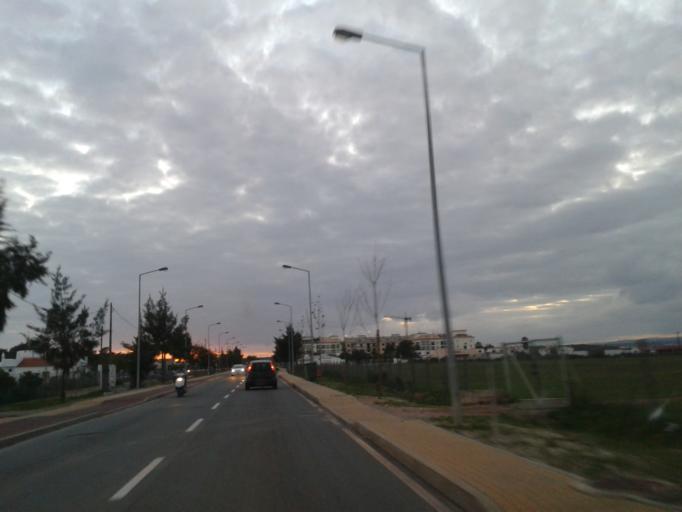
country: PT
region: Faro
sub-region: Vila Real de Santo Antonio
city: Monte Gordo
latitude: 37.1879
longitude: -7.4476
